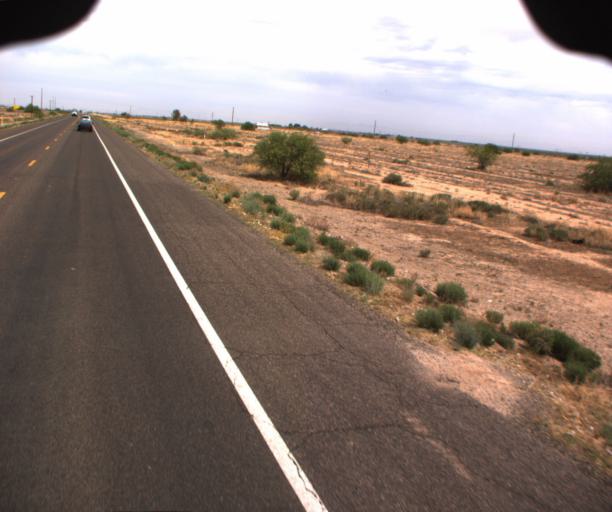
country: US
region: Arizona
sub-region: Pinal County
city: Eloy
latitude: 32.8168
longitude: -111.5153
